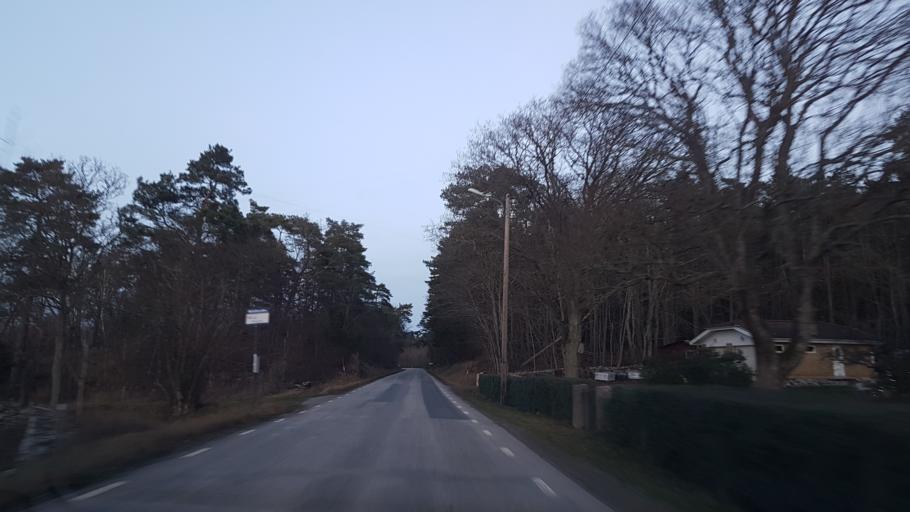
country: SE
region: Blekinge
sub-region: Karlskrona Kommun
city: Jaemjoe
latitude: 56.1229
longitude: 15.8308
